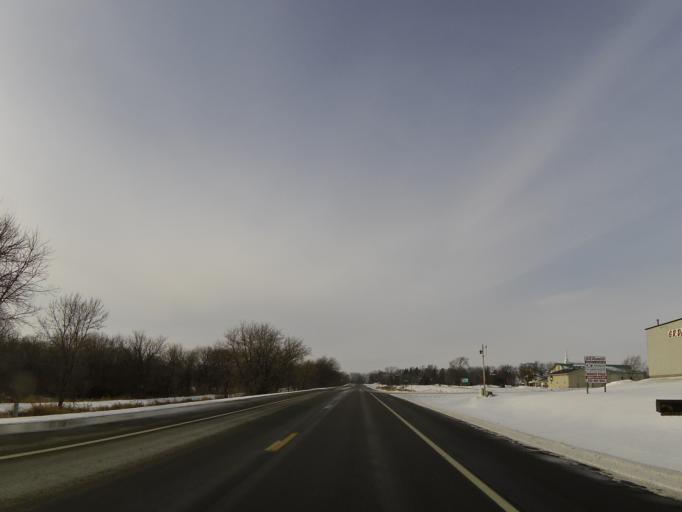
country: US
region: Minnesota
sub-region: McLeod County
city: Hutchinson
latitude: 44.8933
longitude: -94.4150
